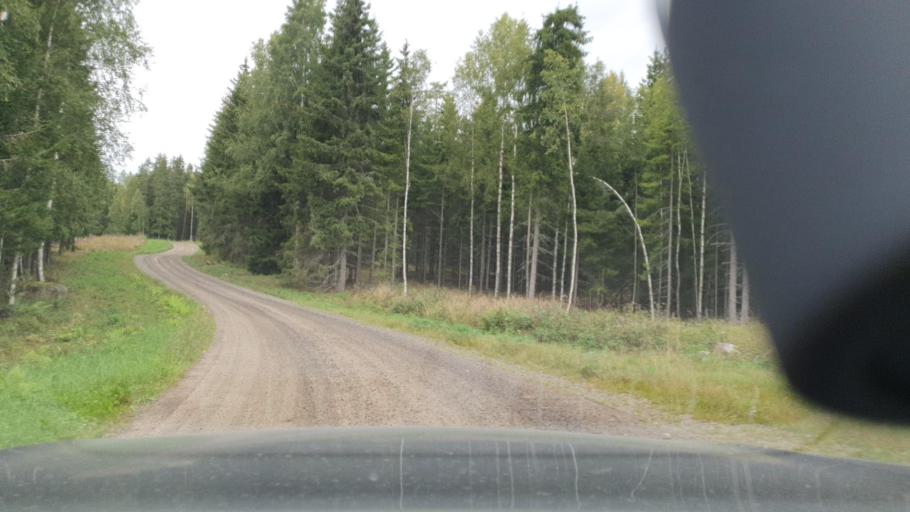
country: SE
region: Vaermland
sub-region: Torsby Kommun
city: Torsby
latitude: 59.9423
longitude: 12.8034
